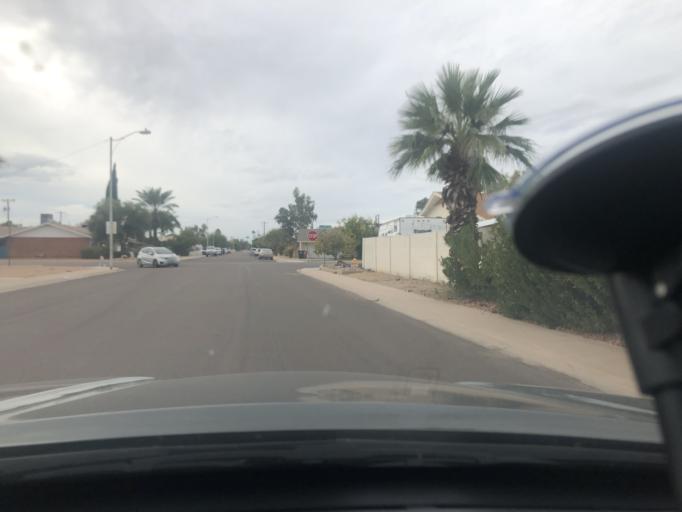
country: US
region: Arizona
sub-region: Maricopa County
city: Scottsdale
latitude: 33.4840
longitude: -111.8997
